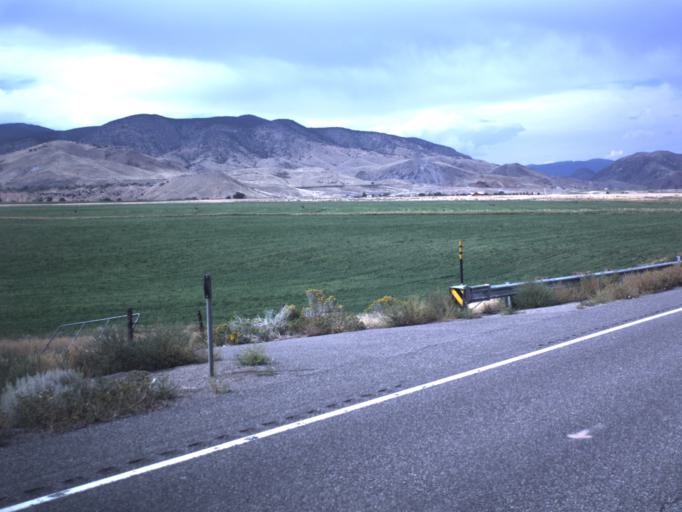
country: US
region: Utah
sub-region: Piute County
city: Junction
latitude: 38.4326
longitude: -112.2313
